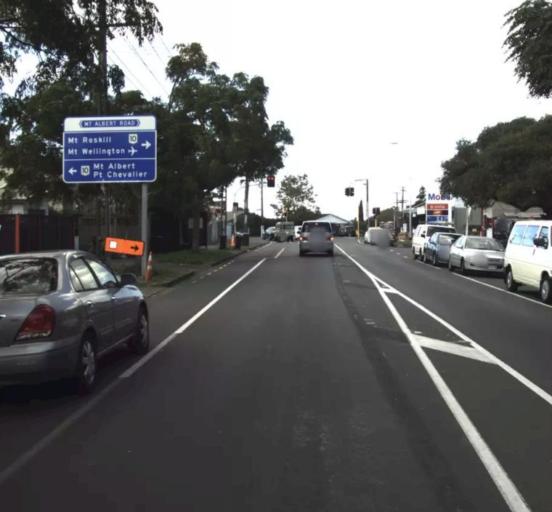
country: NZ
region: Auckland
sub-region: Auckland
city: Auckland
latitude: -36.8941
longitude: 174.7259
